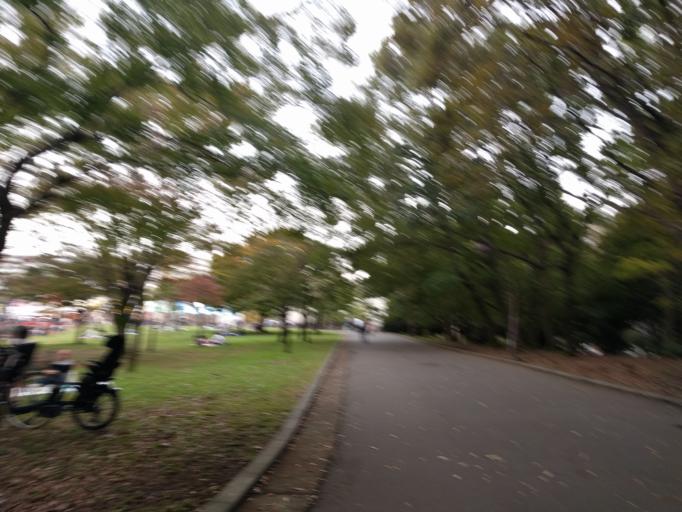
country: JP
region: Saitama
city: Wako
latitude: 35.7633
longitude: 139.6281
